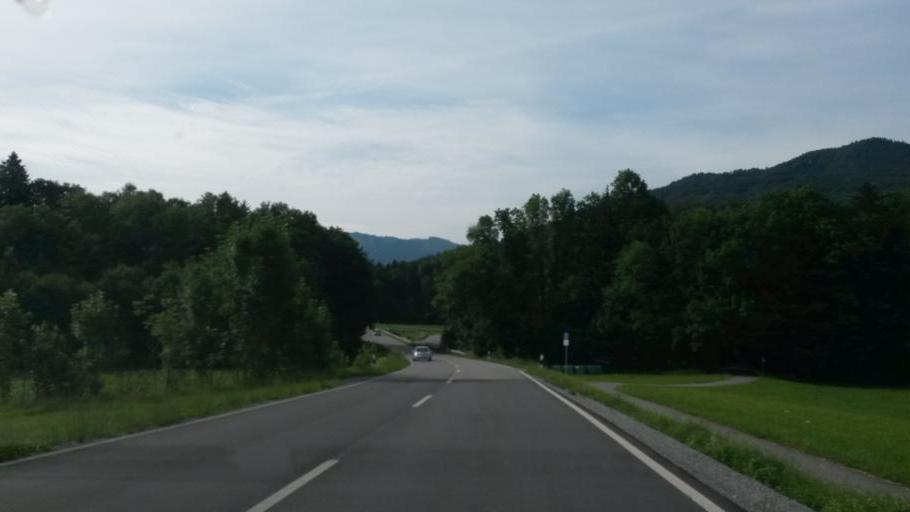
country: DE
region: Bavaria
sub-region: Upper Bavaria
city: Frasdorf
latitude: 47.7992
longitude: 12.2952
